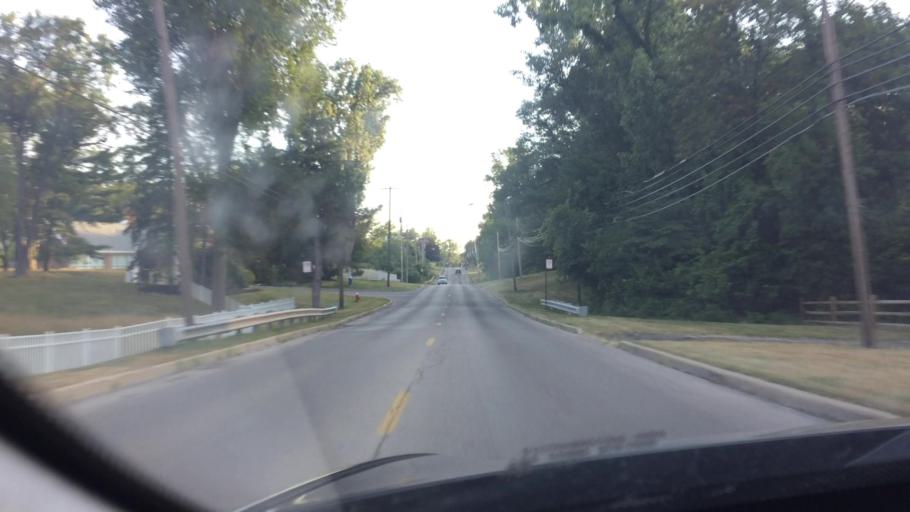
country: US
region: Ohio
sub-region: Lucas County
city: Ottawa Hills
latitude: 41.6551
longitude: -83.6410
